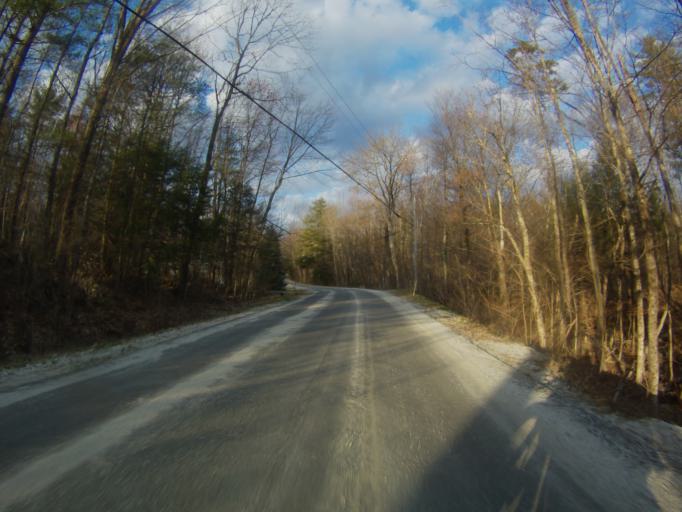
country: US
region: Vermont
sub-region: Rutland County
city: Brandon
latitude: 43.8515
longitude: -73.0178
